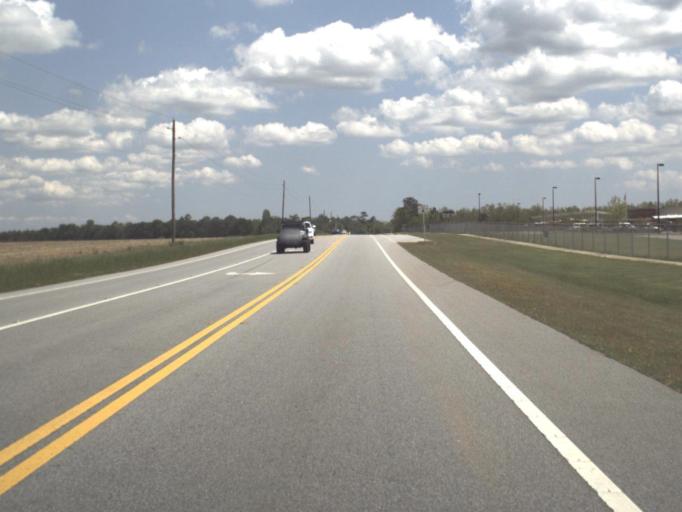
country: US
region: Florida
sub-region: Escambia County
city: Molino
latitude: 30.7427
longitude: -87.3637
